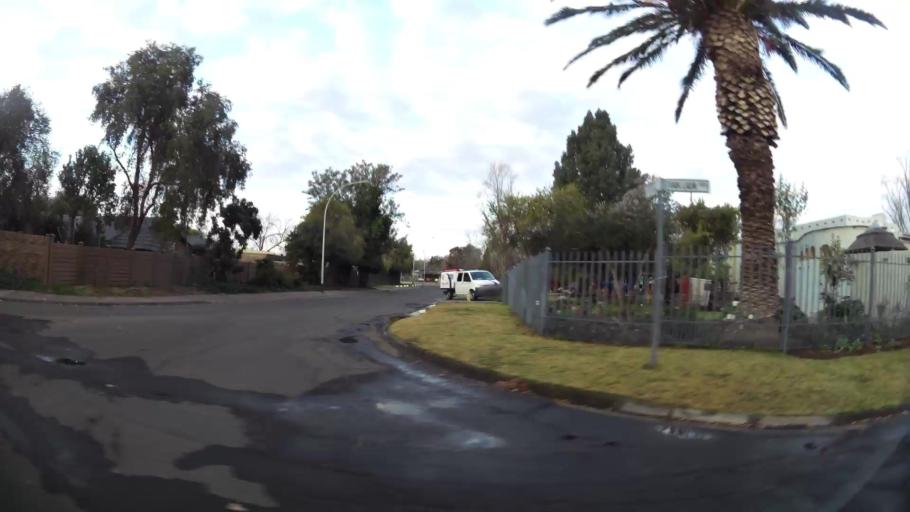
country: ZA
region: Orange Free State
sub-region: Mangaung Metropolitan Municipality
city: Bloemfontein
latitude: -29.1414
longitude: 26.1743
